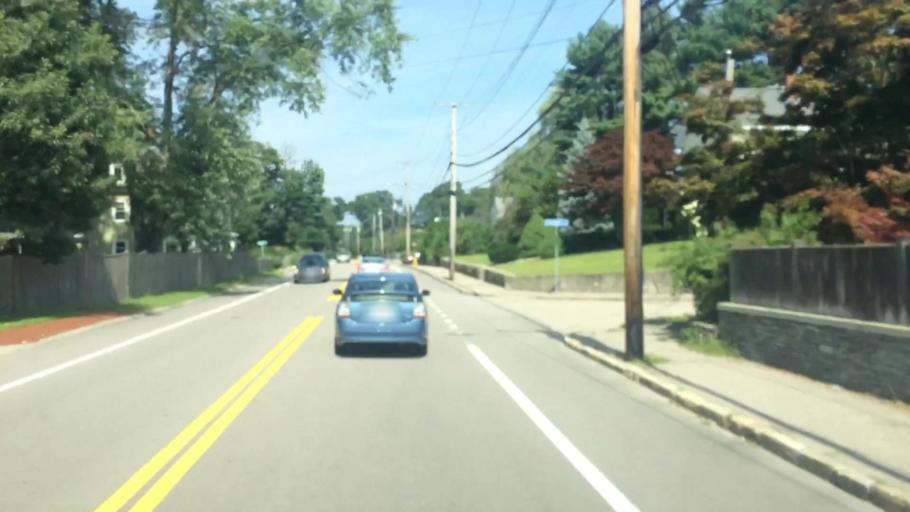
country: US
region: Massachusetts
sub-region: Norfolk County
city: Dedham
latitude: 42.2554
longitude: -71.1773
